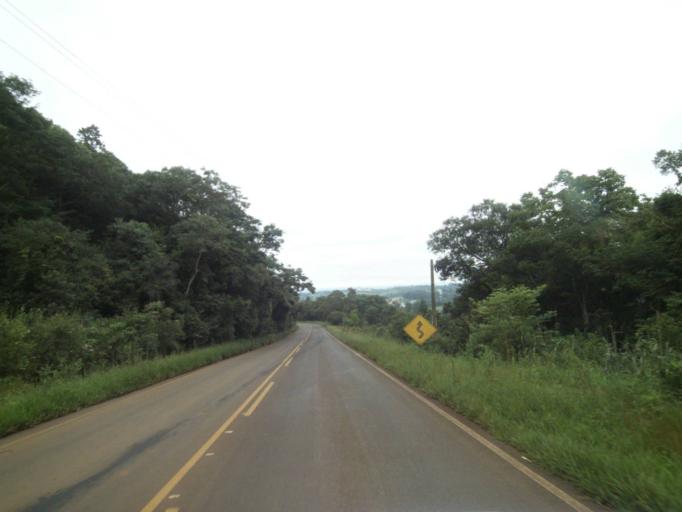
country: BR
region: Parana
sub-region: Pitanga
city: Pitanga
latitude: -24.9166
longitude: -51.8704
